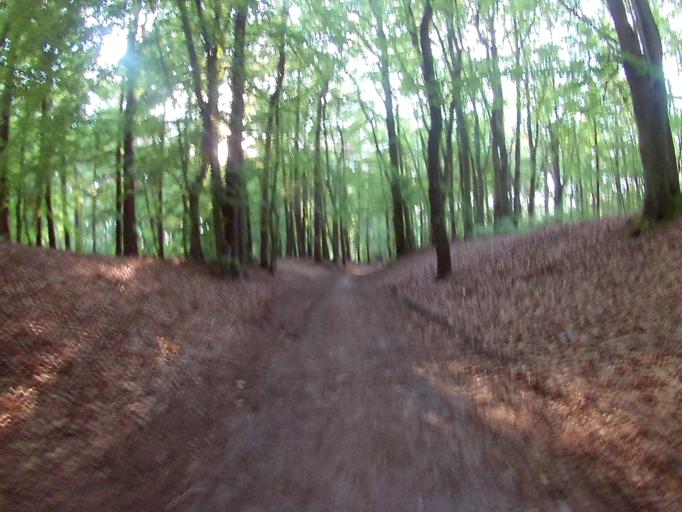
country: DE
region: Mecklenburg-Vorpommern
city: Koserow
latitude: 54.0441
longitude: 14.0132
